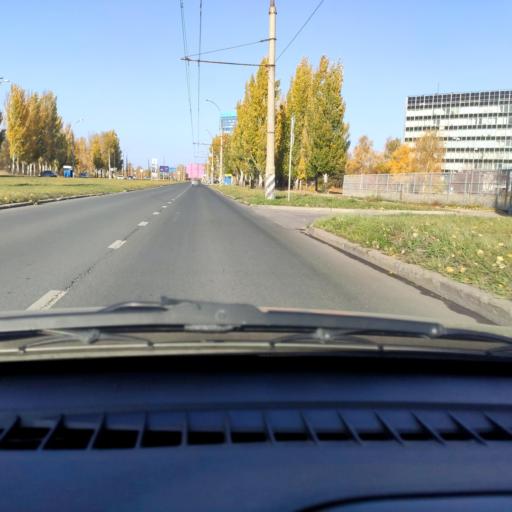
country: RU
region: Samara
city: Tol'yatti
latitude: 53.5500
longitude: 49.2710
